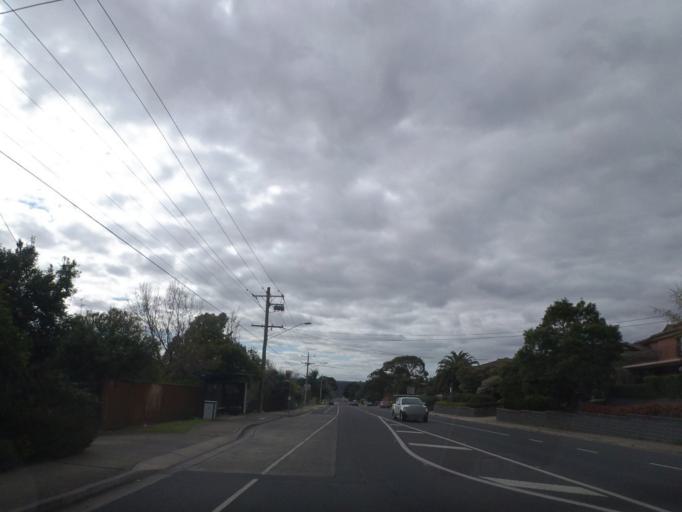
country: AU
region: Victoria
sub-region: Manningham
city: Templestowe Lower
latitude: -37.7652
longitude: 145.1196
